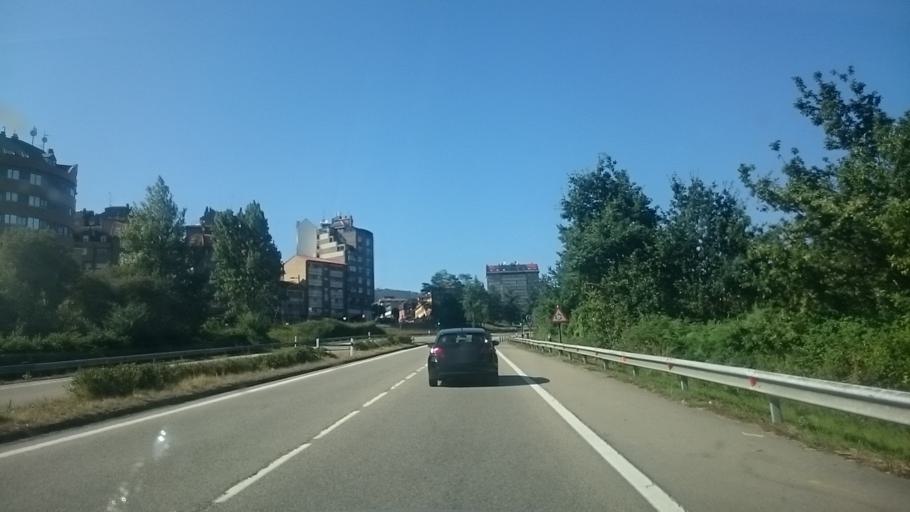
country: ES
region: Asturias
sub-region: Province of Asturias
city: Oviedo
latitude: 43.3539
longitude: -5.8561
